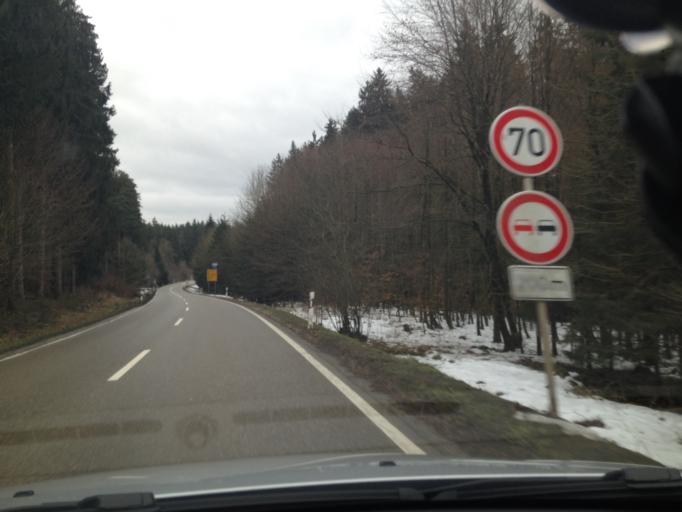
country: DE
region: Bavaria
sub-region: Swabia
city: Adelsried
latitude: 48.4106
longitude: 10.7287
